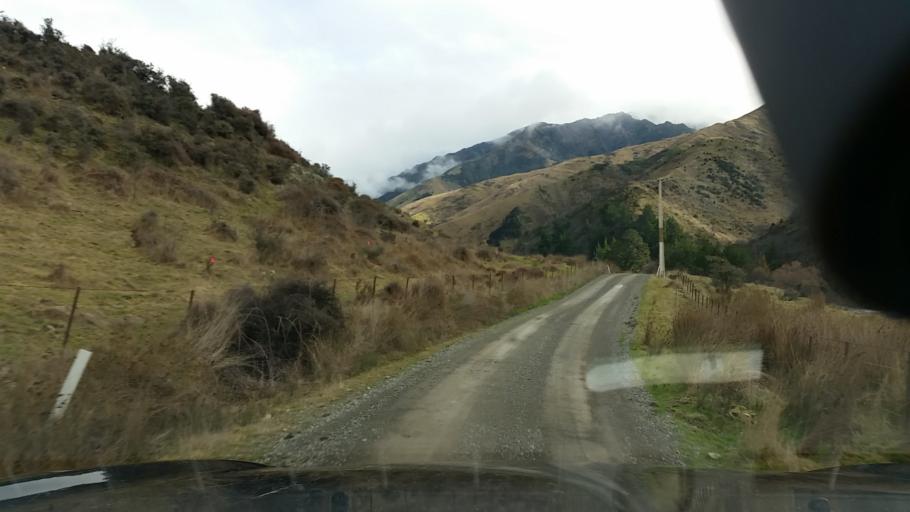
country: NZ
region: Tasman
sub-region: Tasman District
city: Brightwater
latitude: -41.7340
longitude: 173.4316
